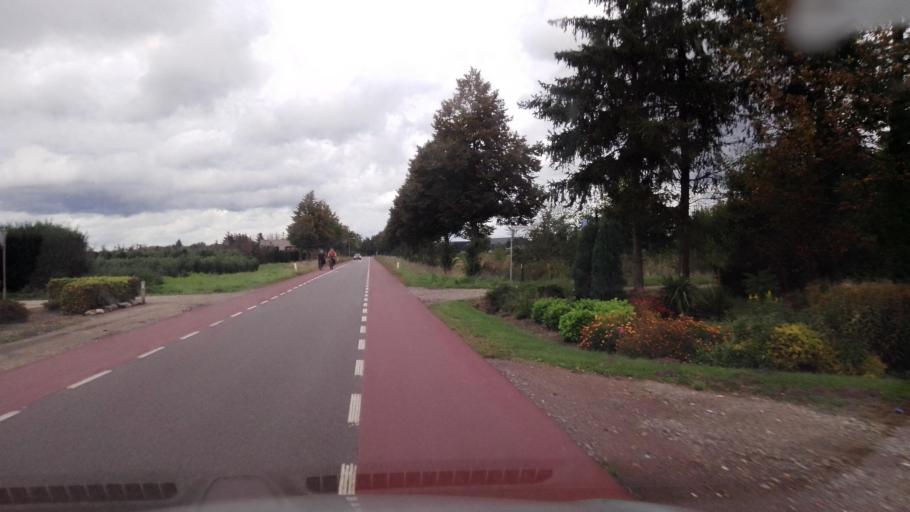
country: NL
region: Limburg
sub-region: Gemeente Peel en Maas
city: Maasbree
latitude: 51.3783
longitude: 6.0510
